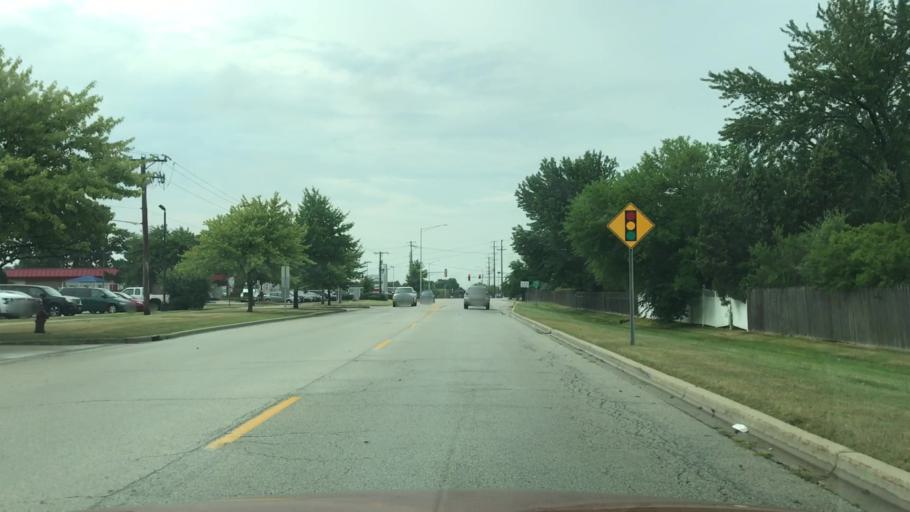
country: US
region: Illinois
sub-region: Cook County
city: Hoffman Estates
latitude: 42.0518
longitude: -88.0995
